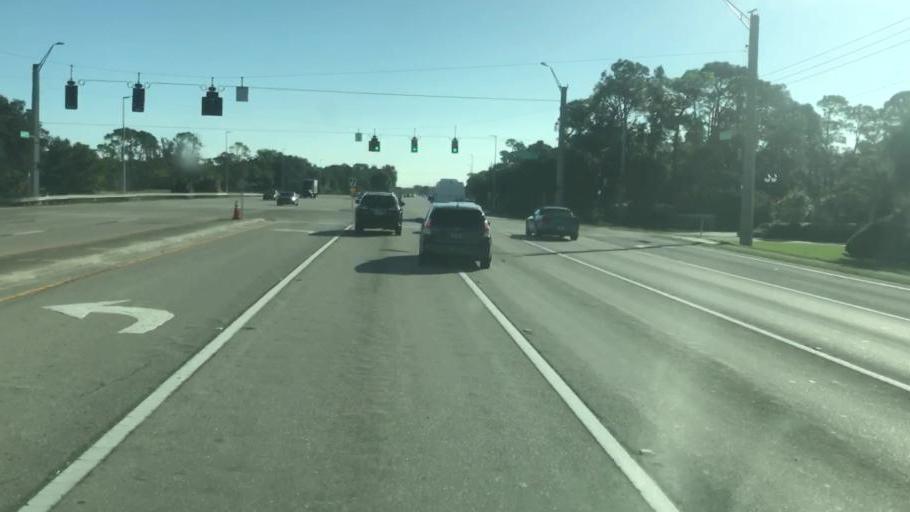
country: US
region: Florida
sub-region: Lee County
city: Villas
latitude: 26.5463
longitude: -81.8643
